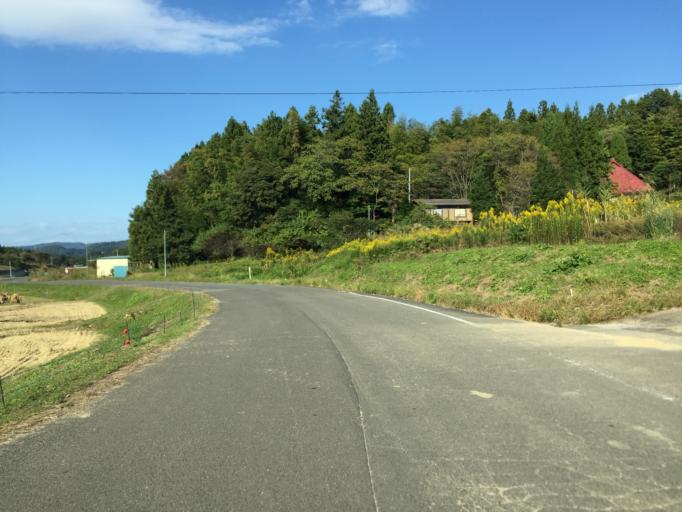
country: JP
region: Fukushima
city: Nihommatsu
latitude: 37.6545
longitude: 140.5000
